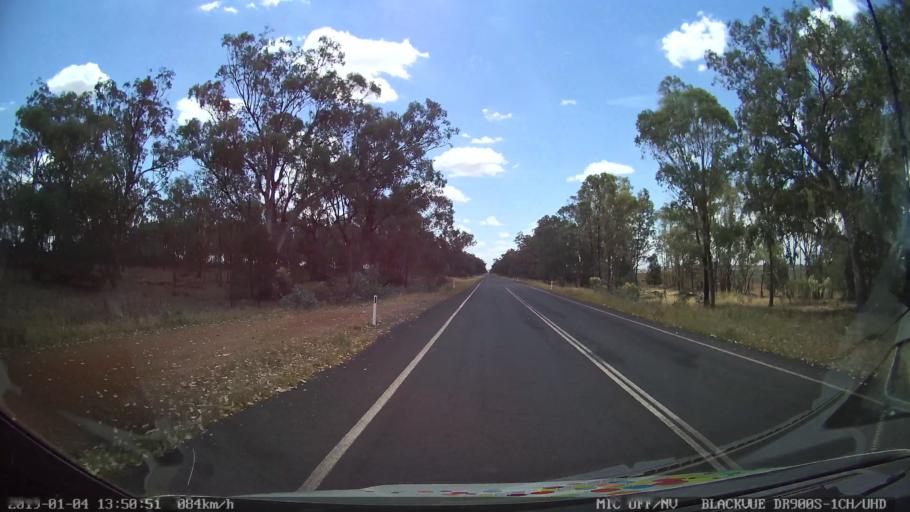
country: AU
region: New South Wales
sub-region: Dubbo Municipality
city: Dubbo
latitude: -32.4149
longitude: 148.5707
